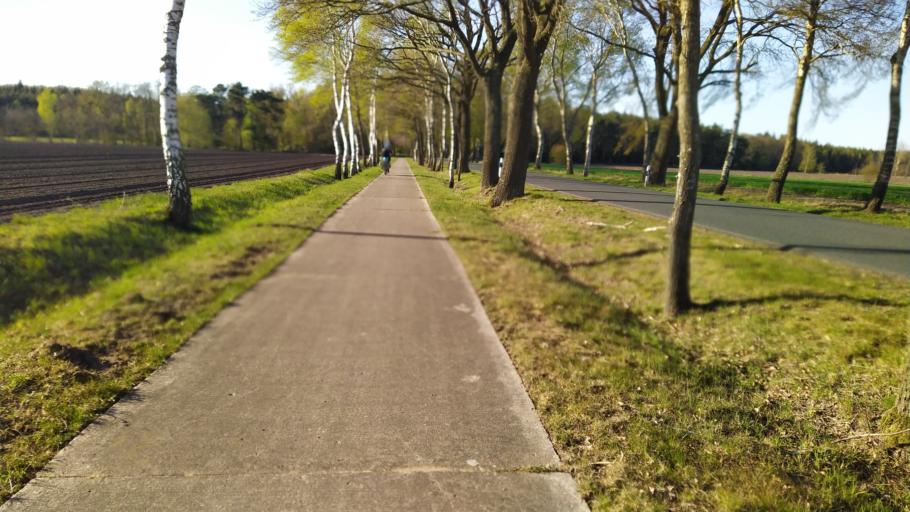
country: DE
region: Lower Saxony
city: Lengenbostel
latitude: 53.3097
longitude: 9.5095
